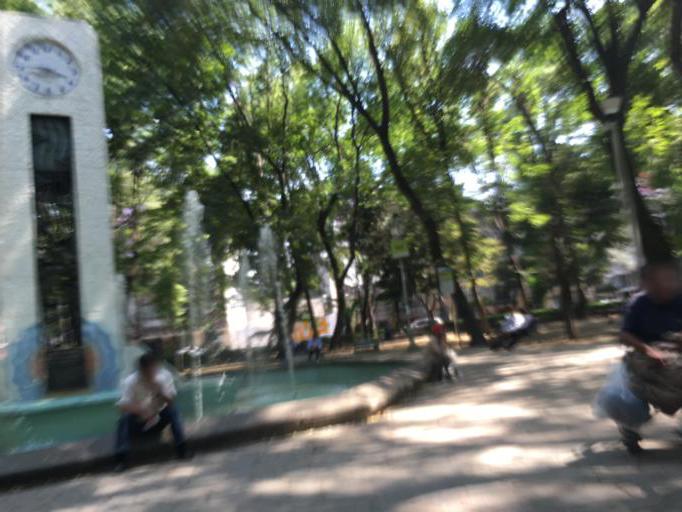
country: MX
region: Mexico City
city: Benito Juarez
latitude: 19.4111
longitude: -99.1701
